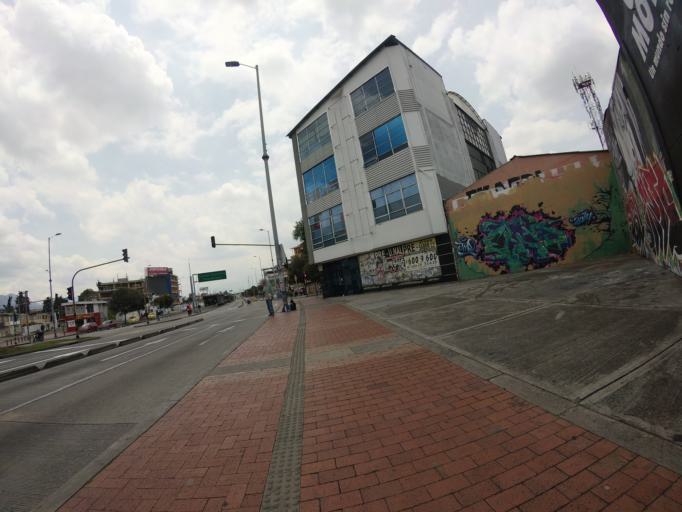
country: CO
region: Bogota D.C.
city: Barrio San Luis
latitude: 4.6817
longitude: -74.0642
